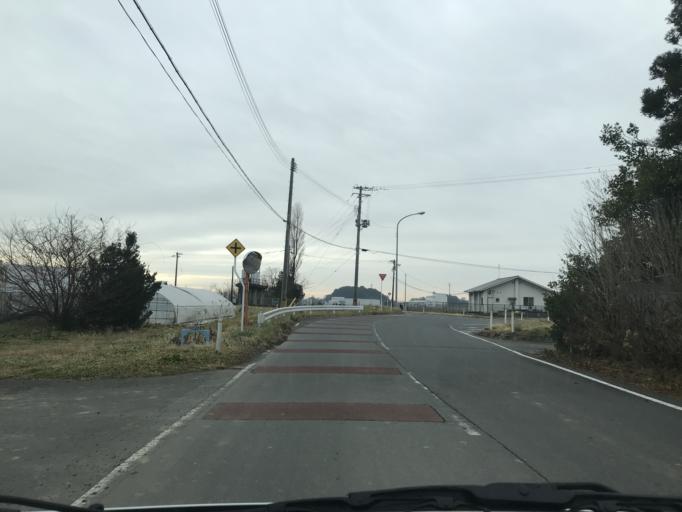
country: JP
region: Iwate
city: Ichinoseki
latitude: 38.7392
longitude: 141.2266
